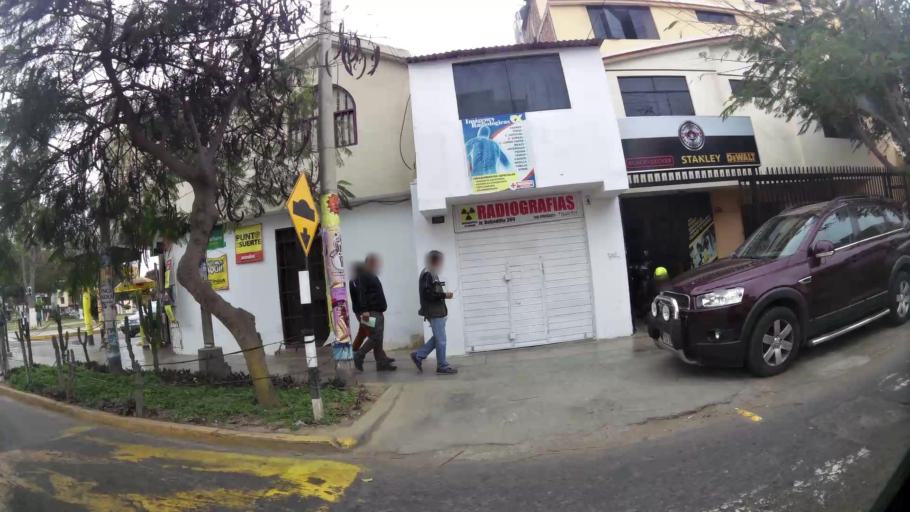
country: PE
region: La Libertad
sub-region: Provincia de Trujillo
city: Trujillo
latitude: -8.1201
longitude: -79.0321
